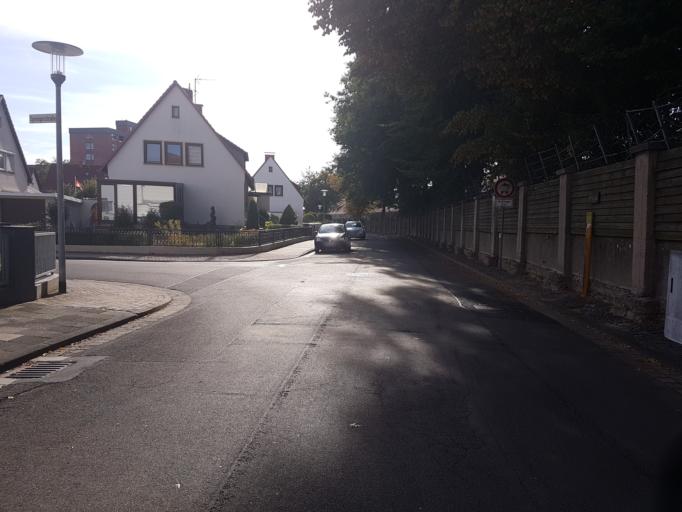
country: DE
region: Lower Saxony
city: Hameln
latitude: 52.1135
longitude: 9.3673
